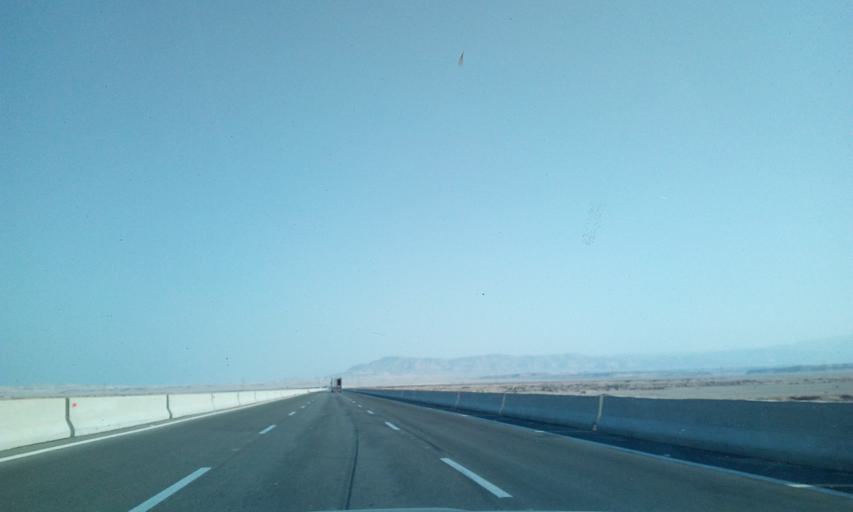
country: EG
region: As Suways
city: Ain Sukhna
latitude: 29.1361
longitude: 32.5217
